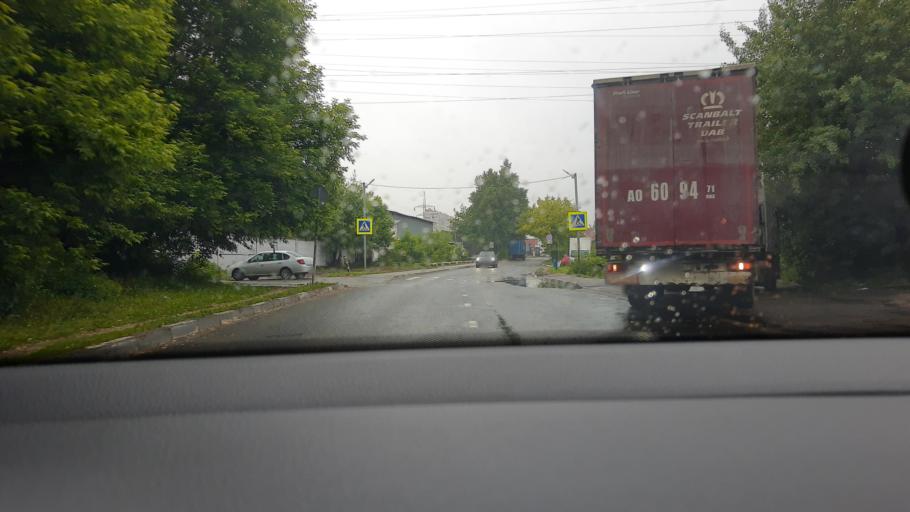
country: RU
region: Moskovskaya
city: Lyubertsy
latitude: 55.6650
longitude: 37.8921
